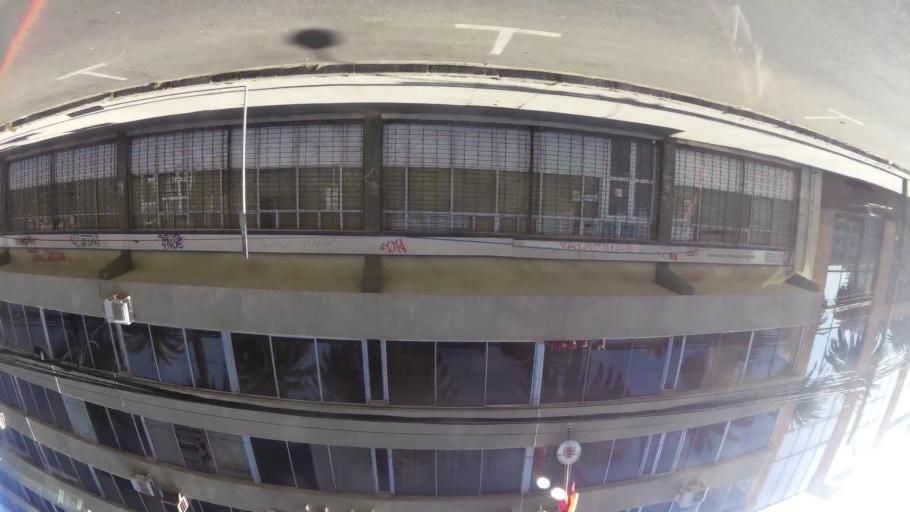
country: CL
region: Valparaiso
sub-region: Provincia de Valparaiso
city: Valparaiso
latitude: -33.0449
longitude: -71.6185
